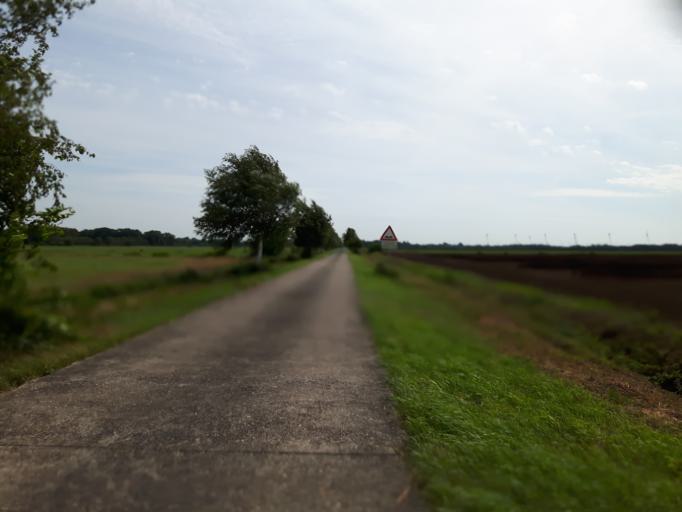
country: DE
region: Lower Saxony
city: Rastede
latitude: 53.2974
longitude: 8.2949
